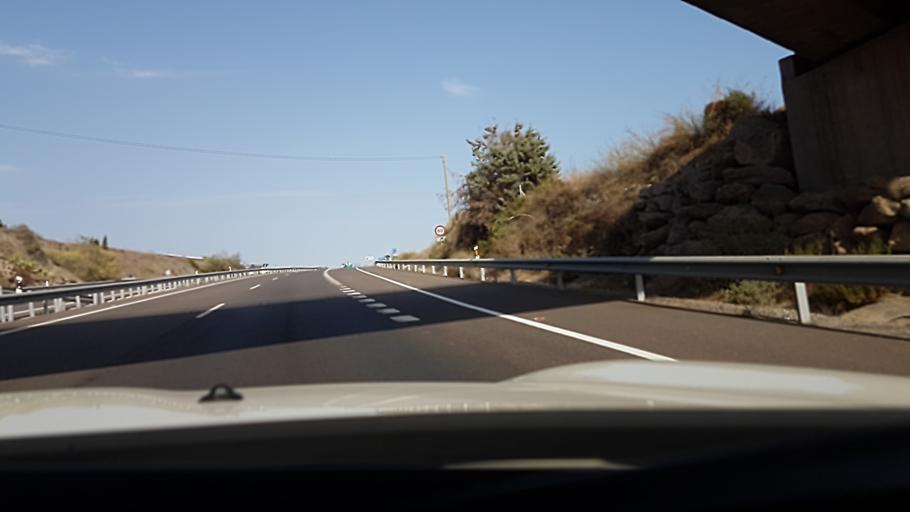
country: ES
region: Andalusia
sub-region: Provincia de Almeria
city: Adra
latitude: 36.7494
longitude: -3.0593
